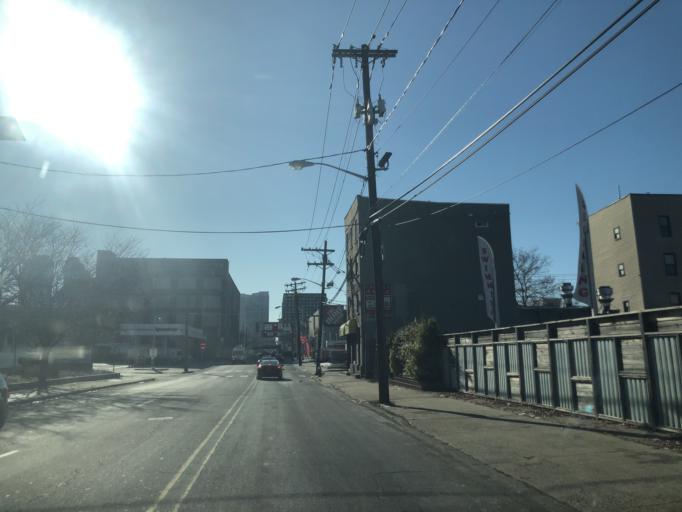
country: US
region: New Jersey
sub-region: Hudson County
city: Hoboken
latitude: 40.7327
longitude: -74.0393
